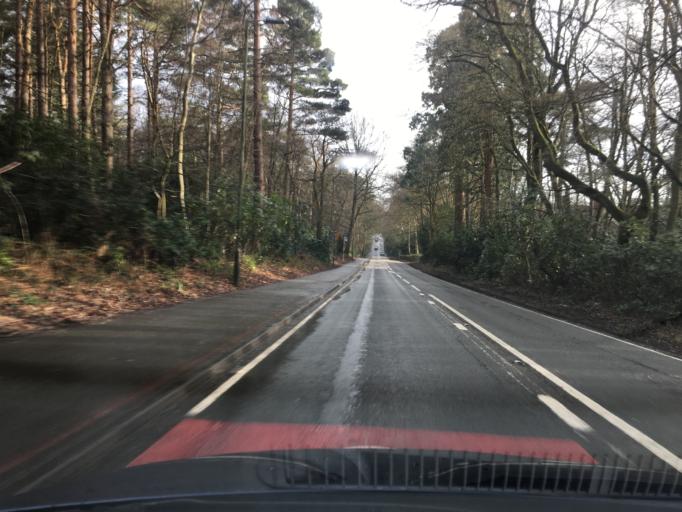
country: GB
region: England
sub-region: Bracknell Forest
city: Crowthorne
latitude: 51.3572
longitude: -0.7984
